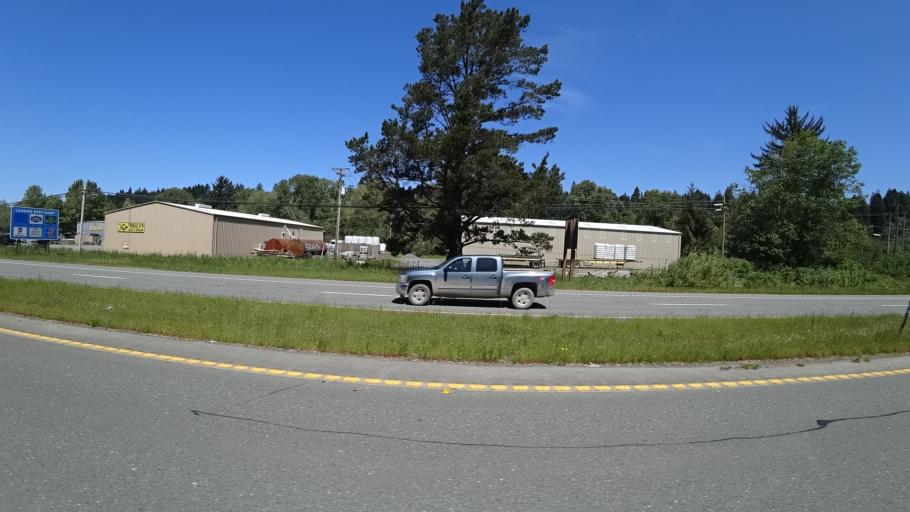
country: US
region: California
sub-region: Humboldt County
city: Arcata
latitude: 40.9104
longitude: -124.0652
